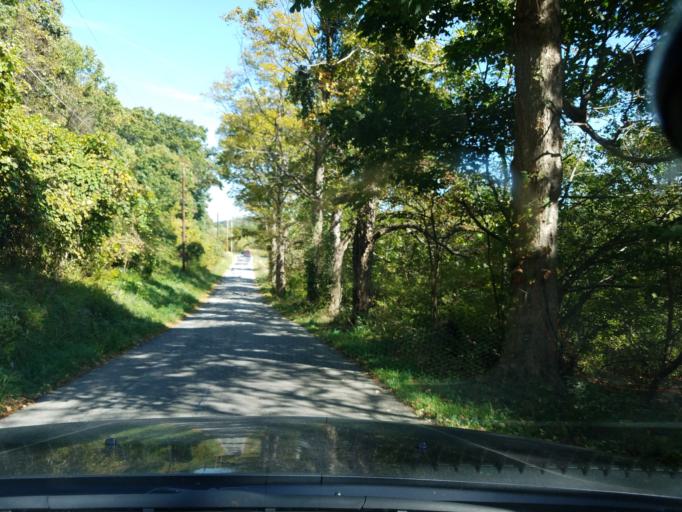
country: US
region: Pennsylvania
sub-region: Lawrence County
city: Ellwood City
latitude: 40.9329
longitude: -80.3056
